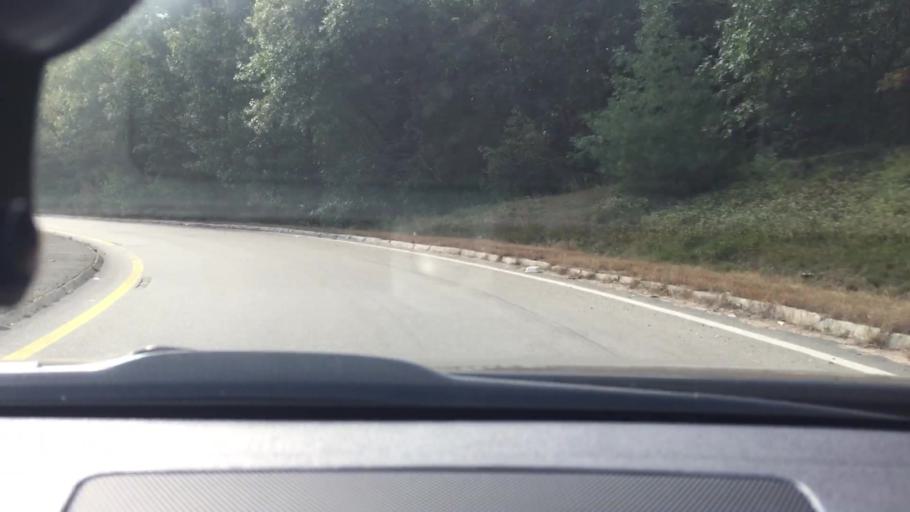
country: US
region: Massachusetts
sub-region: Norfolk County
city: Needham
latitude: 42.2693
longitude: -71.2033
